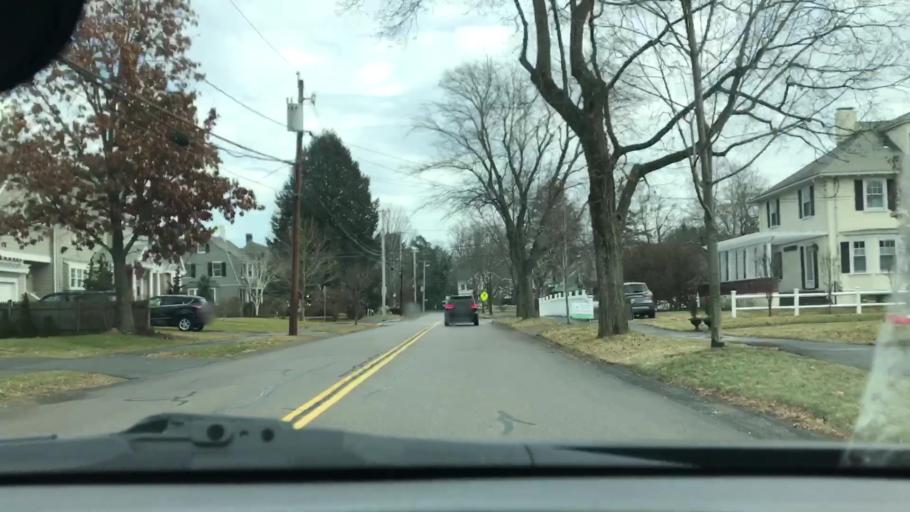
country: US
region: Massachusetts
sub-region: Norfolk County
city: Needham
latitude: 42.2829
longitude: -71.2322
